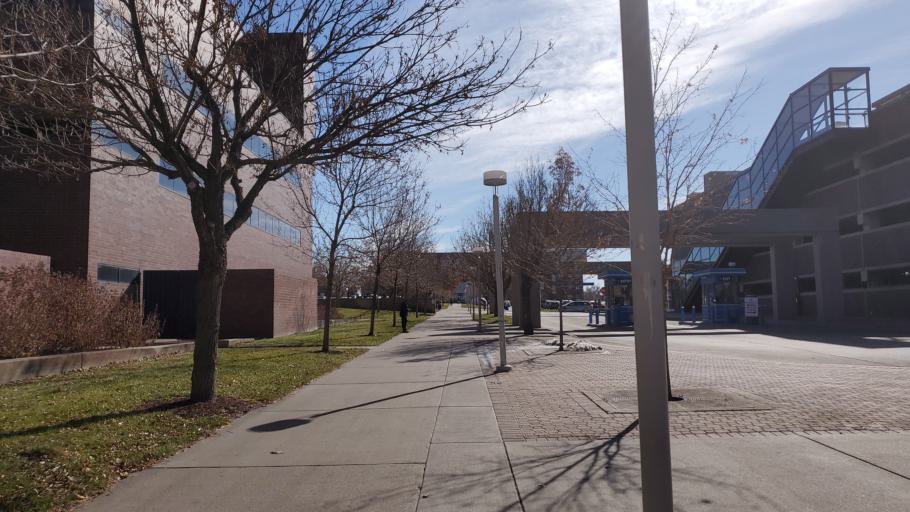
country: US
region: Colorado
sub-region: Denver County
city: Denver
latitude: 39.7436
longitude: -105.0068
